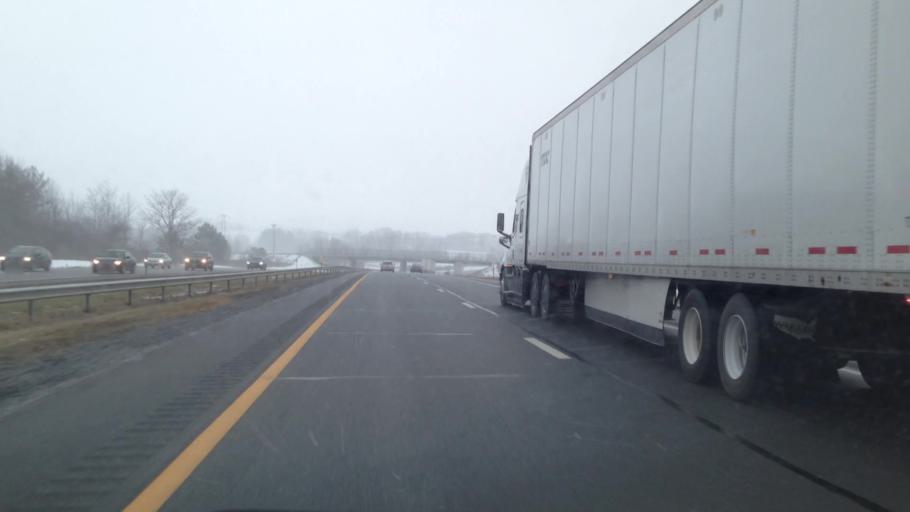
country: US
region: New York
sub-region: Montgomery County
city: Amsterdam
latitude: 42.9019
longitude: -74.1220
